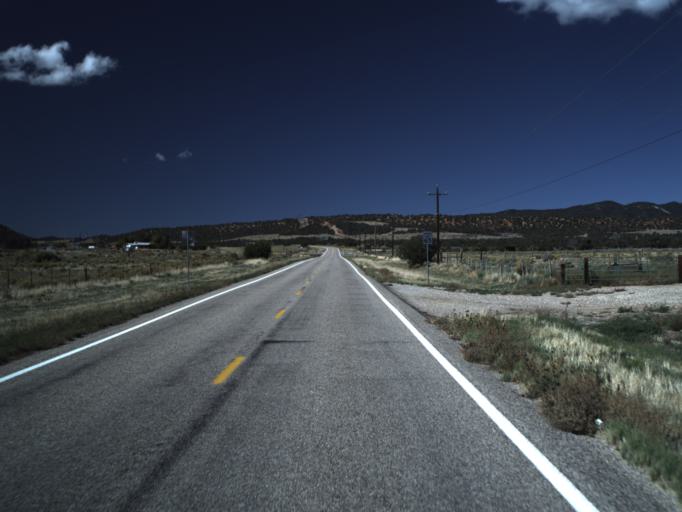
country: US
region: Utah
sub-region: Iron County
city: Cedar City
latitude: 37.6319
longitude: -113.2993
